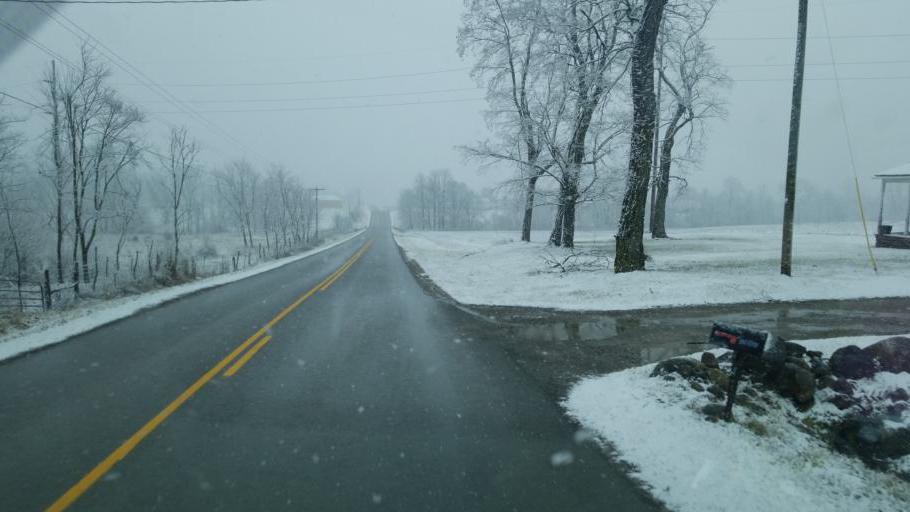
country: US
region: Ohio
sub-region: Champaign County
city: North Lewisburg
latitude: 40.3376
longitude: -83.6059
